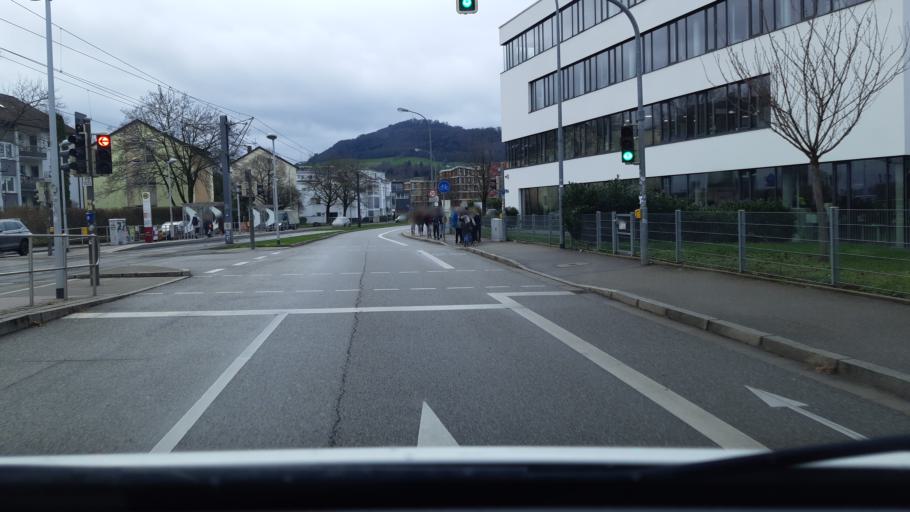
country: DE
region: Baden-Wuerttemberg
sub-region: Freiburg Region
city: Merzhausen
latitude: 47.9790
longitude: 7.8312
